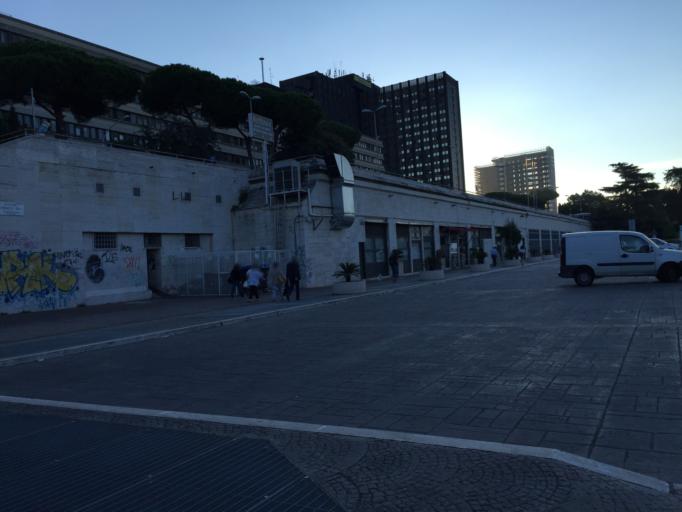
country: IT
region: Latium
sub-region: Citta metropolitana di Roma Capitale
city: Selcetta
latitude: 41.8302
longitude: 12.4650
